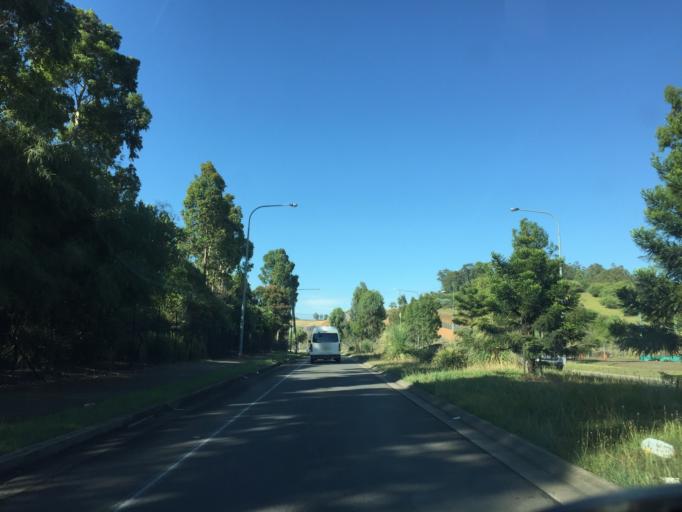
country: AU
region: New South Wales
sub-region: Holroyd
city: Girraween
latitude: -33.8175
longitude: 150.9200
